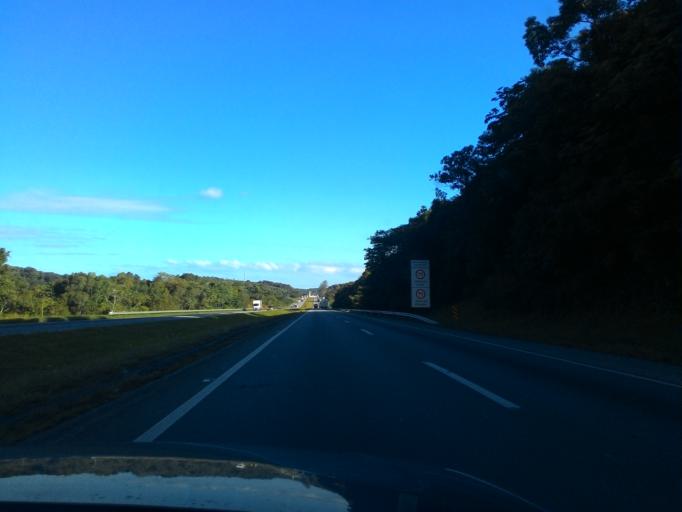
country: BR
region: Sao Paulo
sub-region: Registro
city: Registro
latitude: -24.5430
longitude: -47.8612
